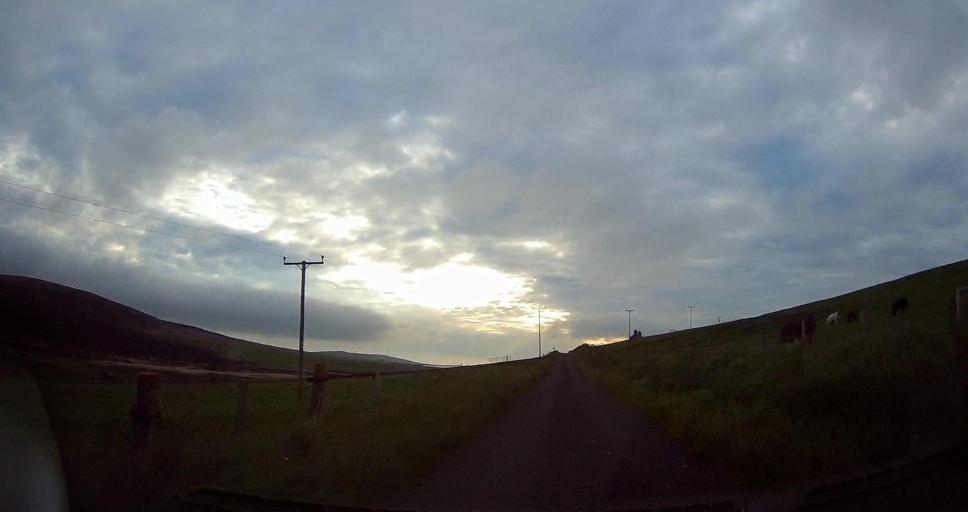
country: GB
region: Scotland
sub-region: Orkney Islands
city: Stromness
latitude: 59.1005
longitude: -3.2057
